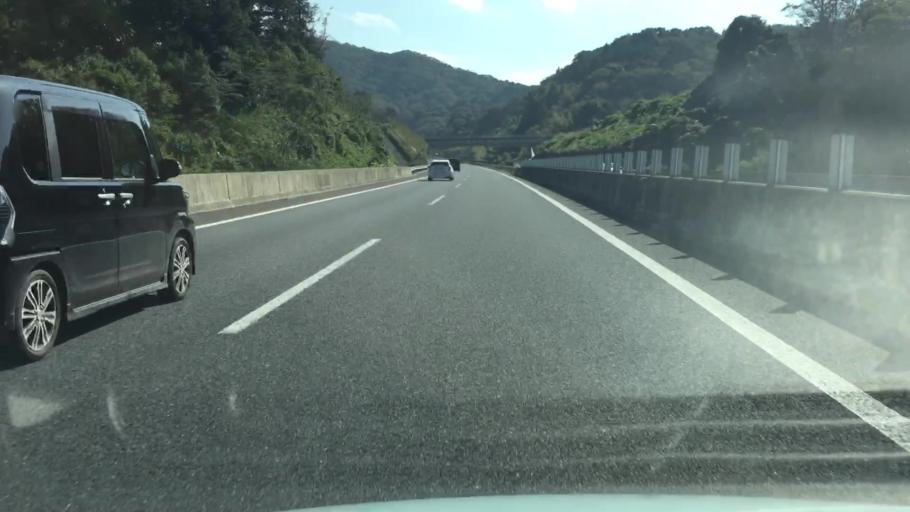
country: JP
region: Ibaraki
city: Kasama
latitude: 36.3411
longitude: 140.2229
